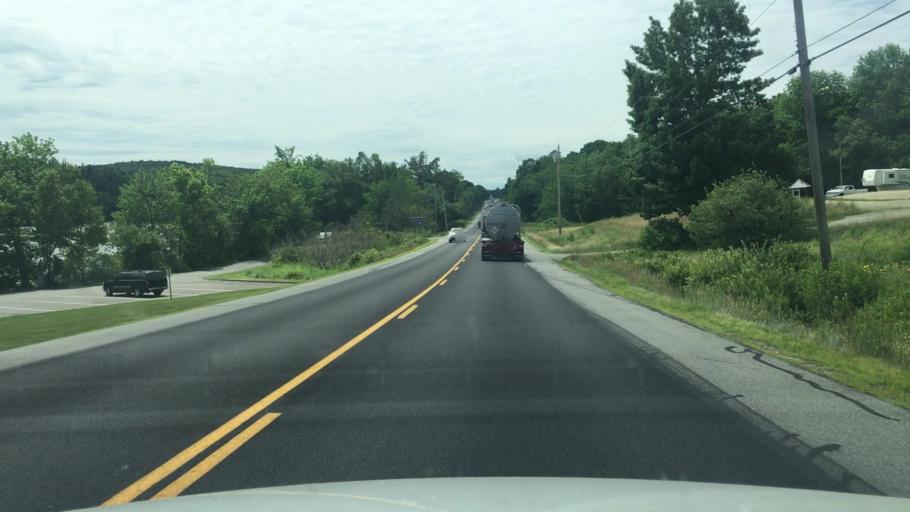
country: US
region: Maine
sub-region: Knox County
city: Washington
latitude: 44.3951
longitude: -69.3509
